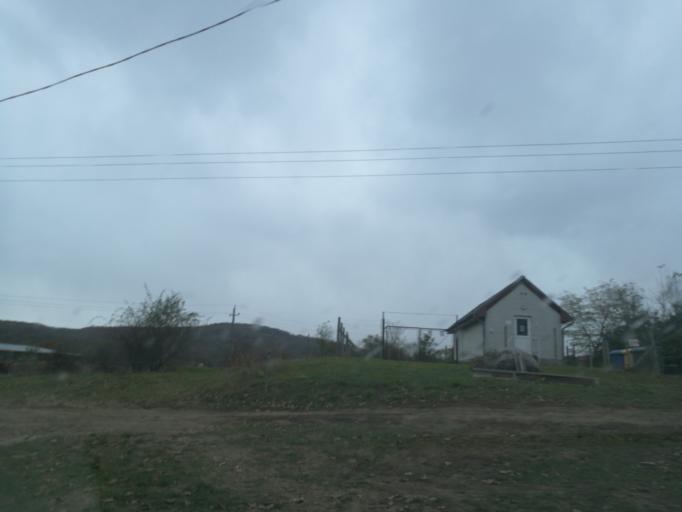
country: HU
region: Nograd
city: Paszto
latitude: 47.9784
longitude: 19.6360
